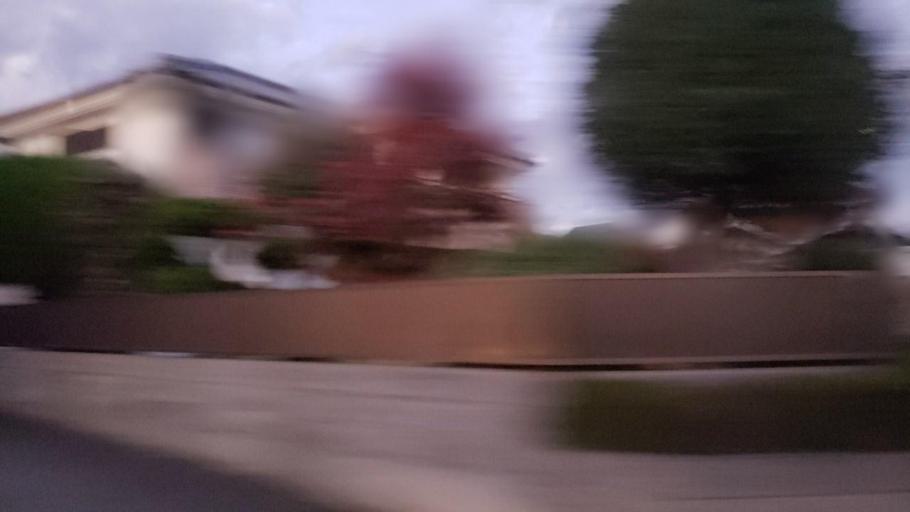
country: JP
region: Tokushima
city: Kamojimacho-jogejima
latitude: 34.0879
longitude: 134.2912
